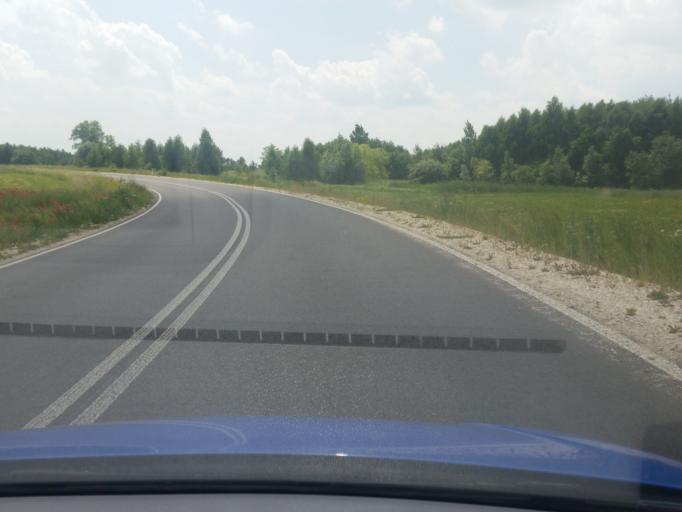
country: PL
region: Swietokrzyskie
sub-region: Powiat buski
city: Busko-Zdroj
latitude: 50.4129
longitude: 20.6986
